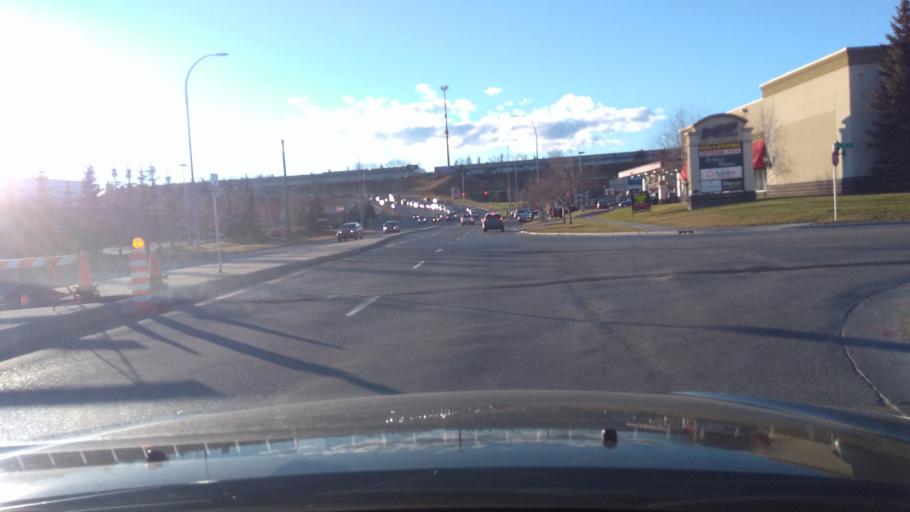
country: CA
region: Alberta
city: Calgary
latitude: 50.9873
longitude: -114.0418
